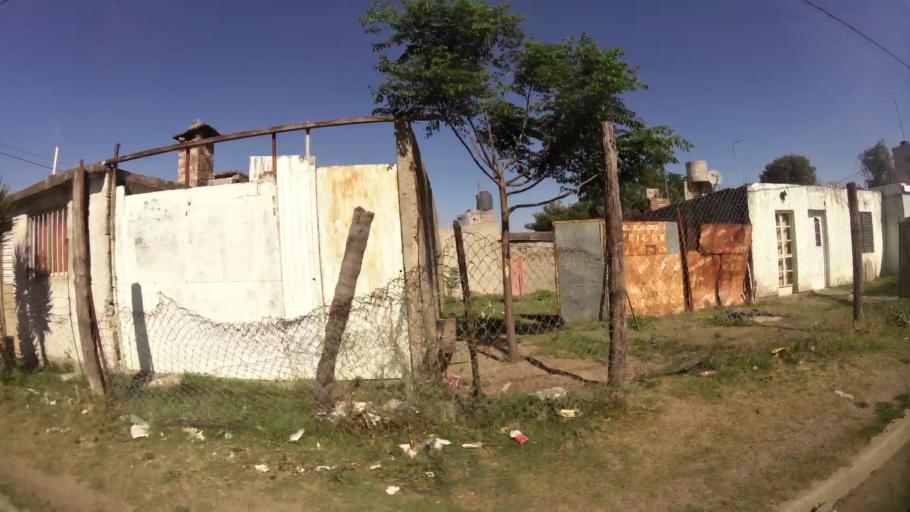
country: AR
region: Cordoba
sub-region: Departamento de Capital
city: Cordoba
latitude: -31.3731
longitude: -64.1936
